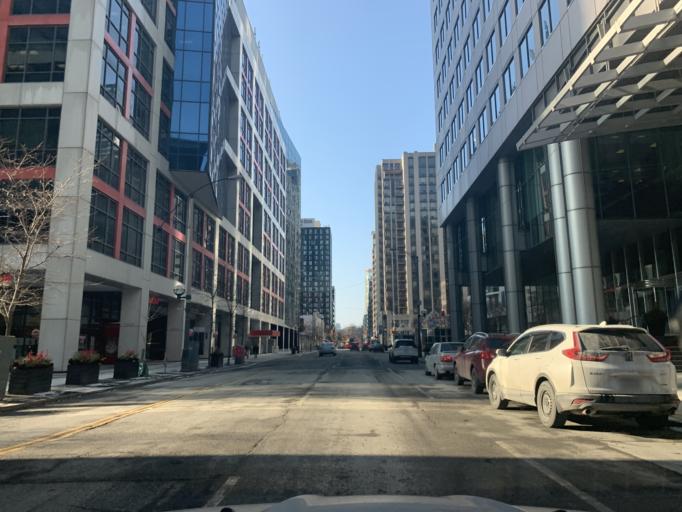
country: CA
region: Ontario
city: Toronto
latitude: 43.6456
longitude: -79.3874
